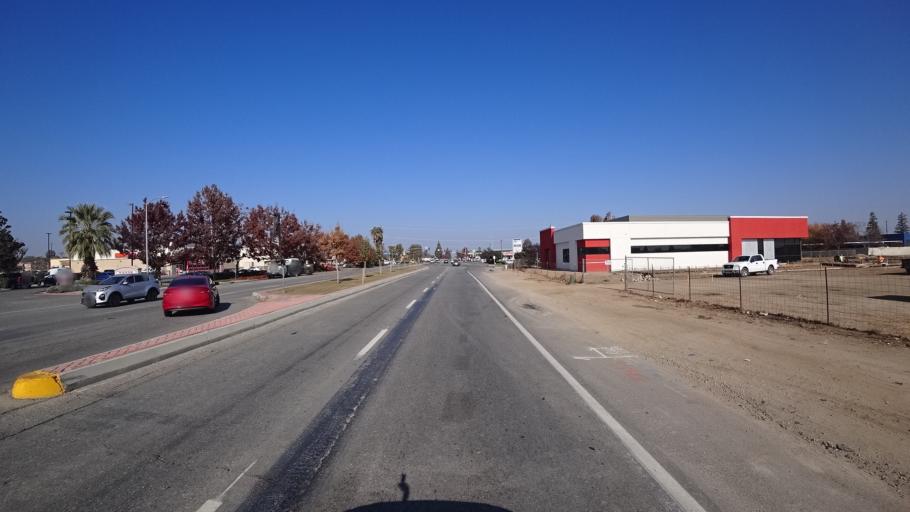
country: US
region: California
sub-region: Kern County
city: Greenfield
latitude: 35.2943
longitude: -119.0388
